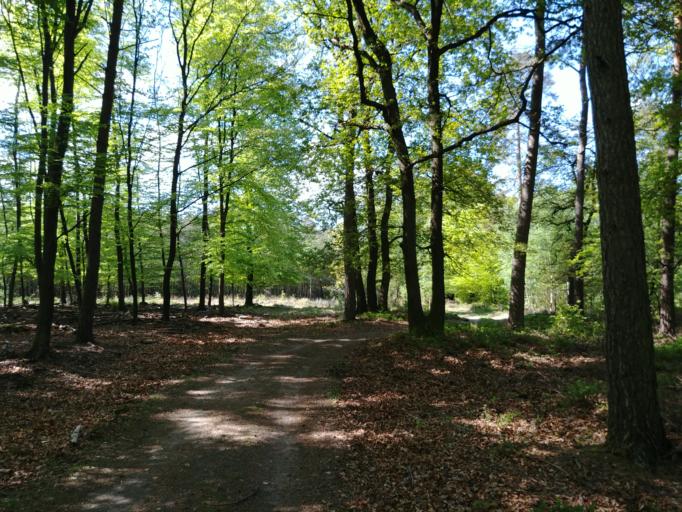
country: NL
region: Gelderland
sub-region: Gemeente Apeldoorn
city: Uddel
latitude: 52.2551
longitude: 5.8619
